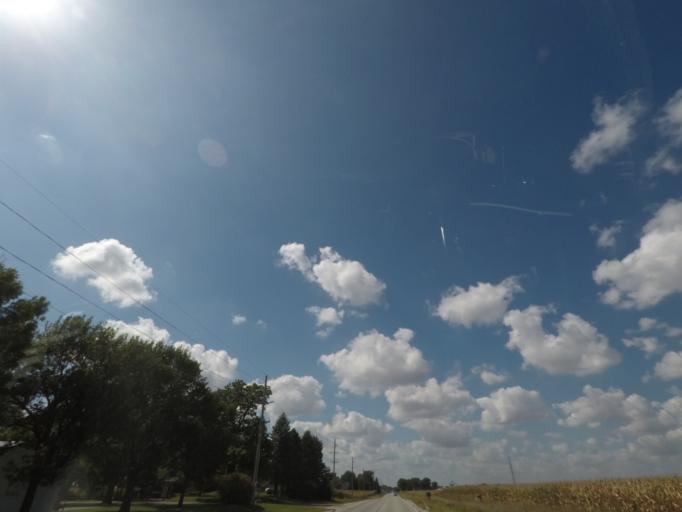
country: US
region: Iowa
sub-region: Story County
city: Nevada
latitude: 42.0227
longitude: -93.4218
